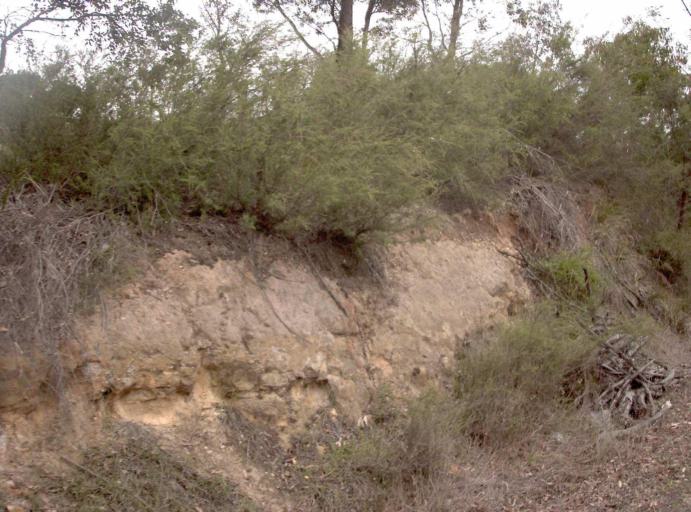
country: AU
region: Victoria
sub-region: East Gippsland
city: Bairnsdale
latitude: -37.7566
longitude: 147.5991
